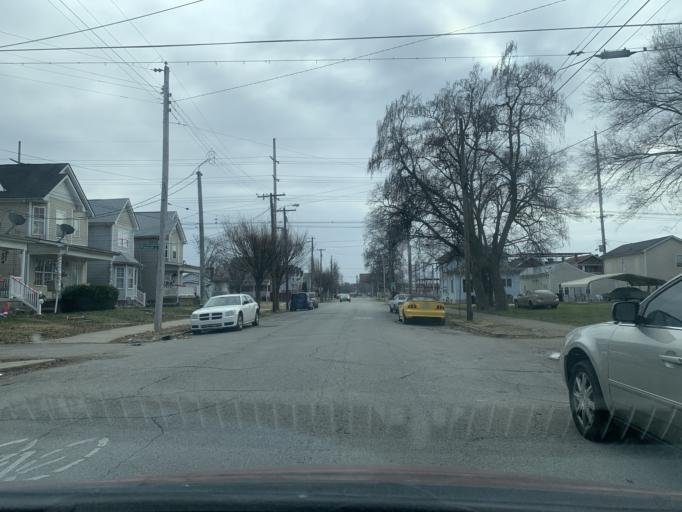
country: US
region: Kentucky
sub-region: Jefferson County
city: Louisville
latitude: 38.2512
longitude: -85.7828
